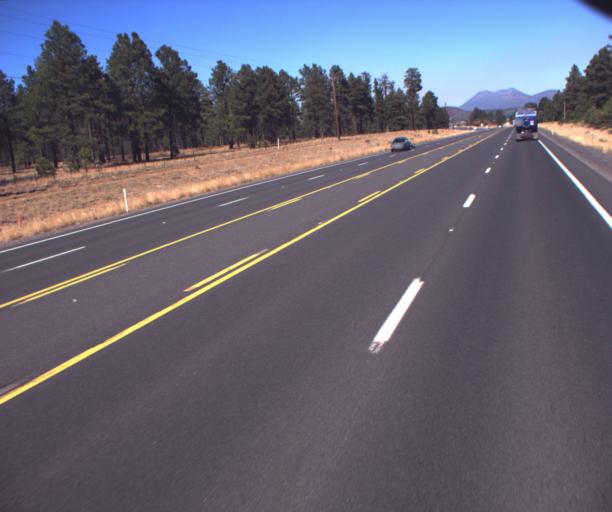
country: US
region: Arizona
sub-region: Coconino County
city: Flagstaff
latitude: 35.2800
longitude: -111.5425
